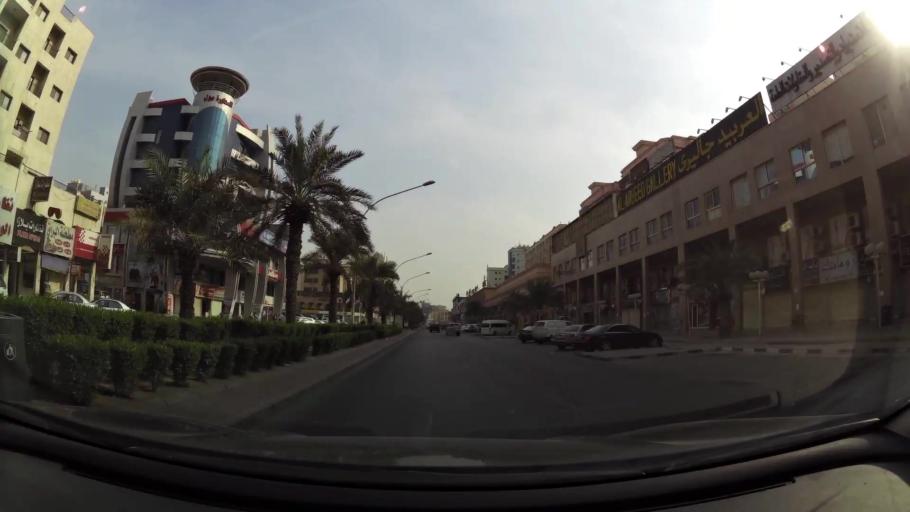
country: KW
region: Al Farwaniyah
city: Al Farwaniyah
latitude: 29.2764
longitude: 47.9629
